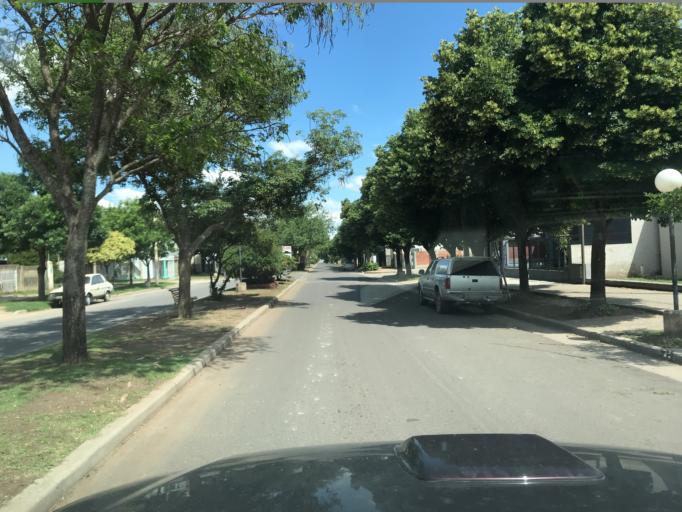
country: AR
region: Cordoba
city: Las Perdices
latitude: -32.7525
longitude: -63.7853
